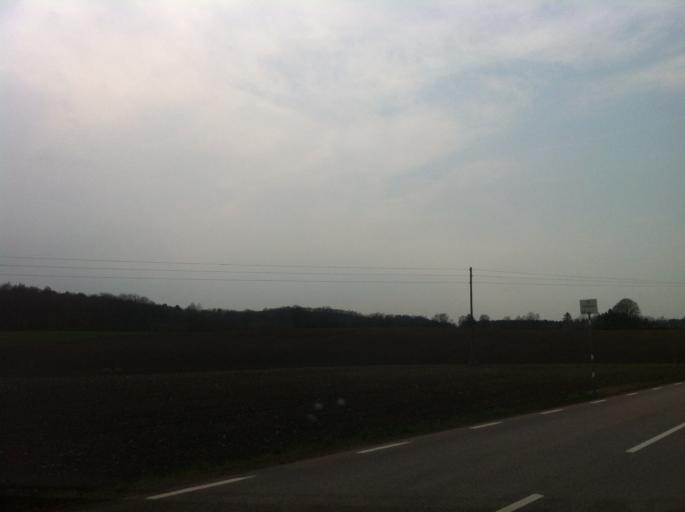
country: SE
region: Skane
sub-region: Klippans Kommun
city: Ljungbyhed
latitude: 55.9916
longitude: 13.2369
